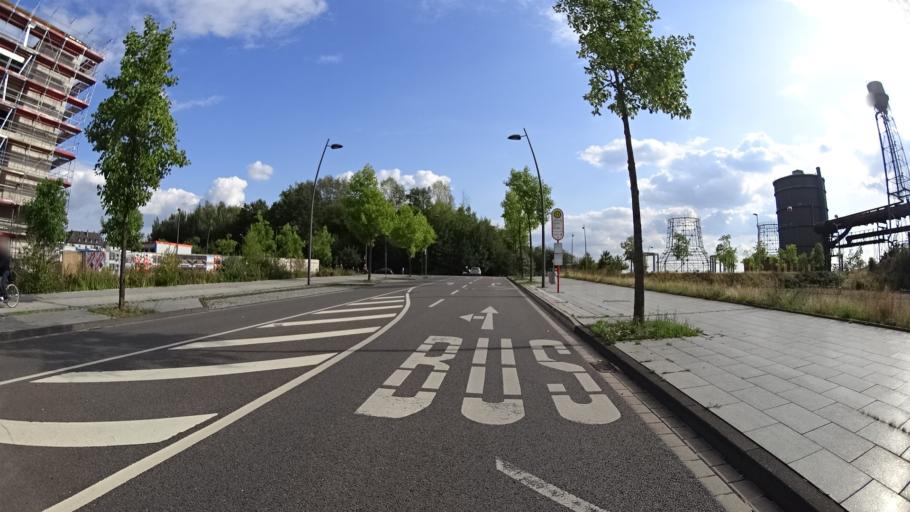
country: DE
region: North Rhine-Westphalia
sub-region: Regierungsbezirk Arnsberg
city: Dortmund
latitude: 51.4876
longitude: 7.4878
